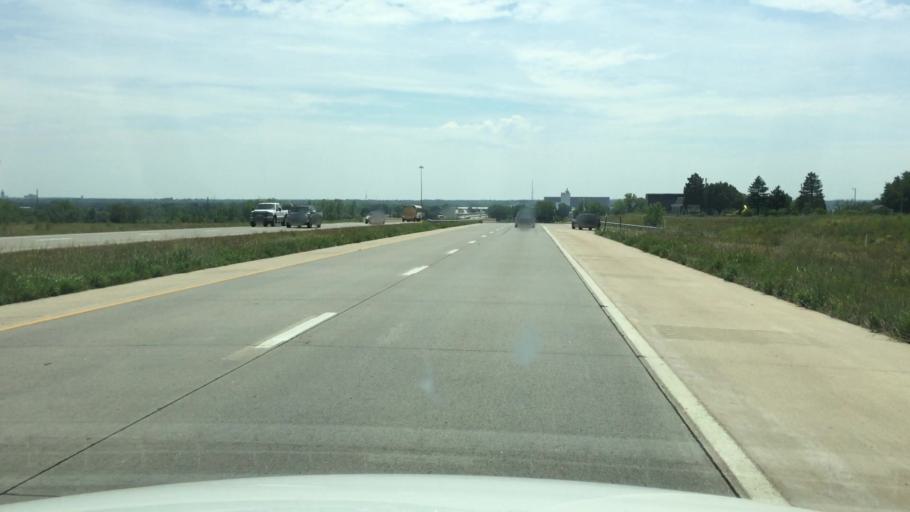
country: US
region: Kansas
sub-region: Shawnee County
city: Topeka
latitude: 39.1107
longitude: -95.7208
